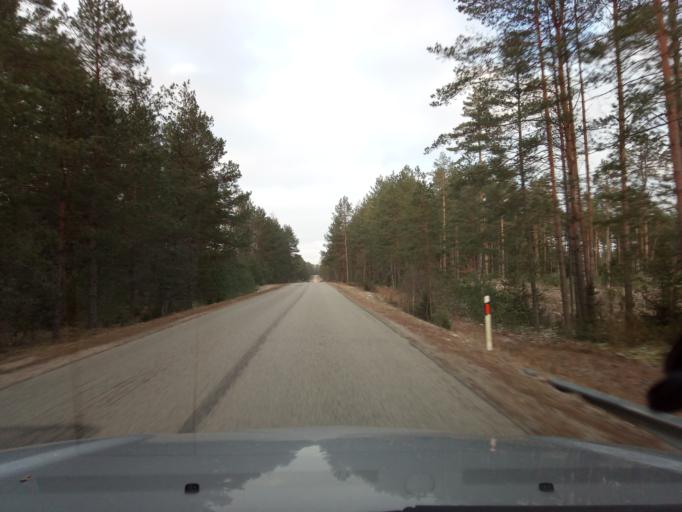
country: LT
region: Alytaus apskritis
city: Varena
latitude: 54.1888
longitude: 24.5219
